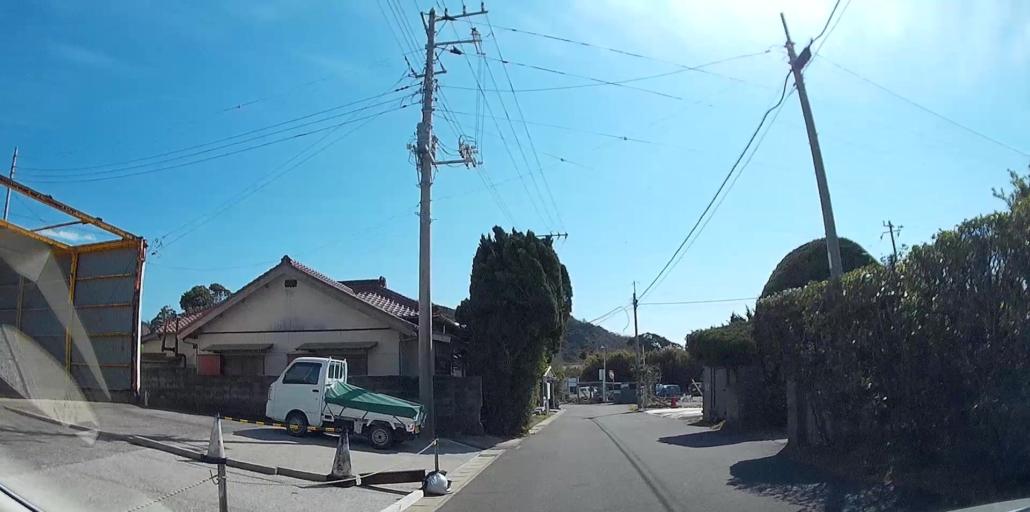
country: JP
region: Chiba
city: Tateyama
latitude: 34.9750
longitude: 139.7569
